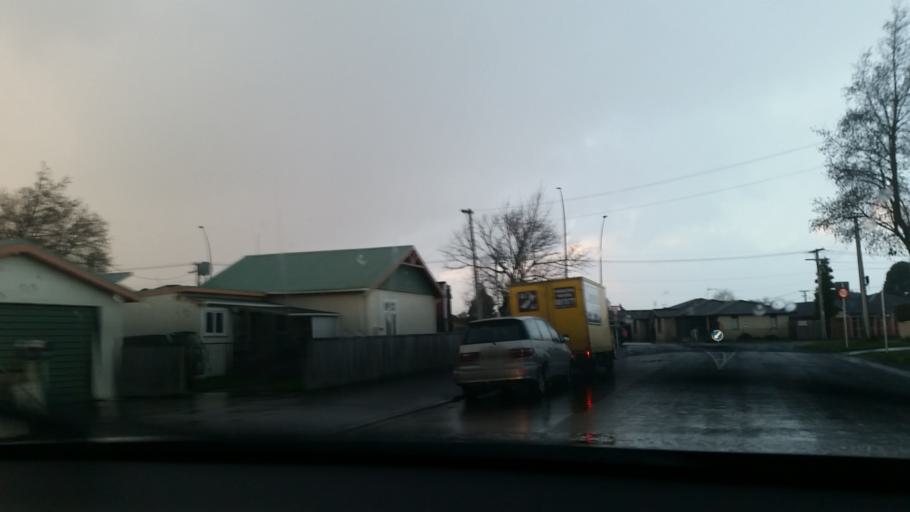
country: NZ
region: Waikato
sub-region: Hamilton City
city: Hamilton
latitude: -37.7958
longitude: 175.2555
